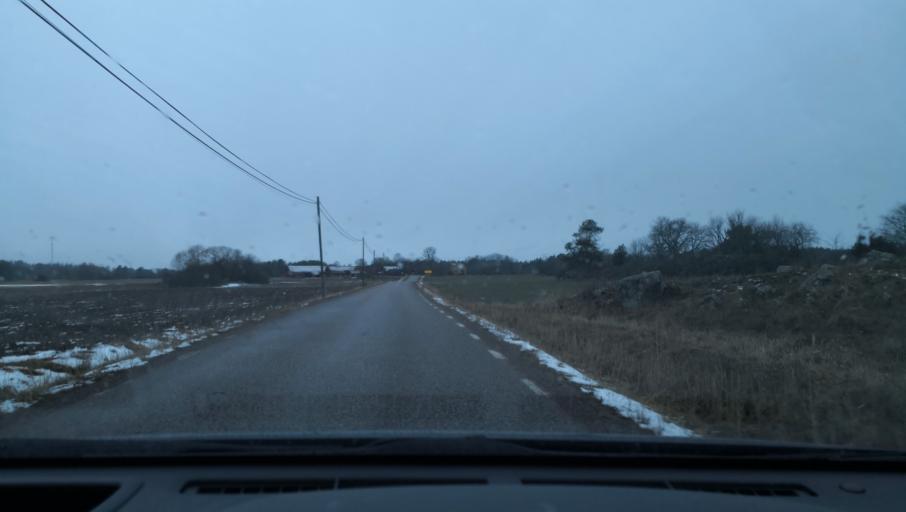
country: SE
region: Soedermanland
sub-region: Strangnas Kommun
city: Strangnas
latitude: 59.4507
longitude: 16.8684
